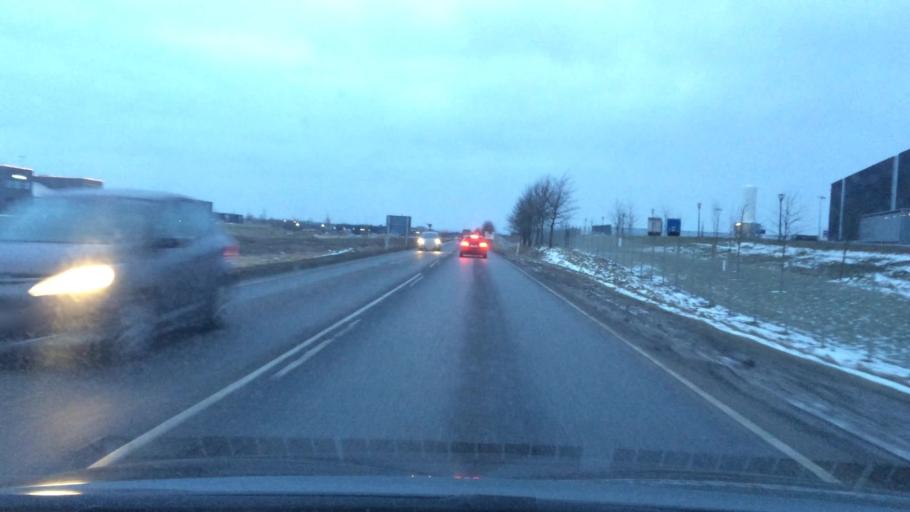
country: DK
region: Central Jutland
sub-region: Horsens Kommune
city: Horsens
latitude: 55.8347
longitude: 9.7963
